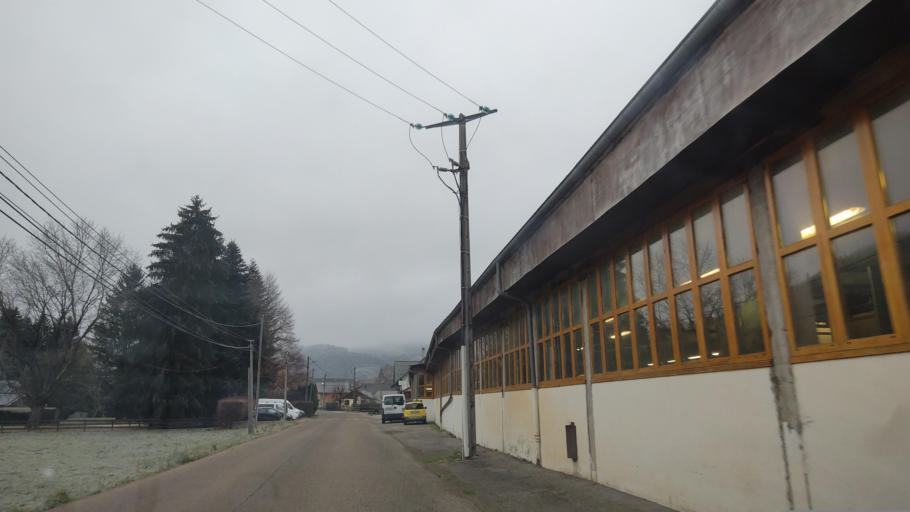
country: FR
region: Rhone-Alpes
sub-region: Departement de la Savoie
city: Gresy-sur-Isere
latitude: 45.6454
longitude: 6.1651
